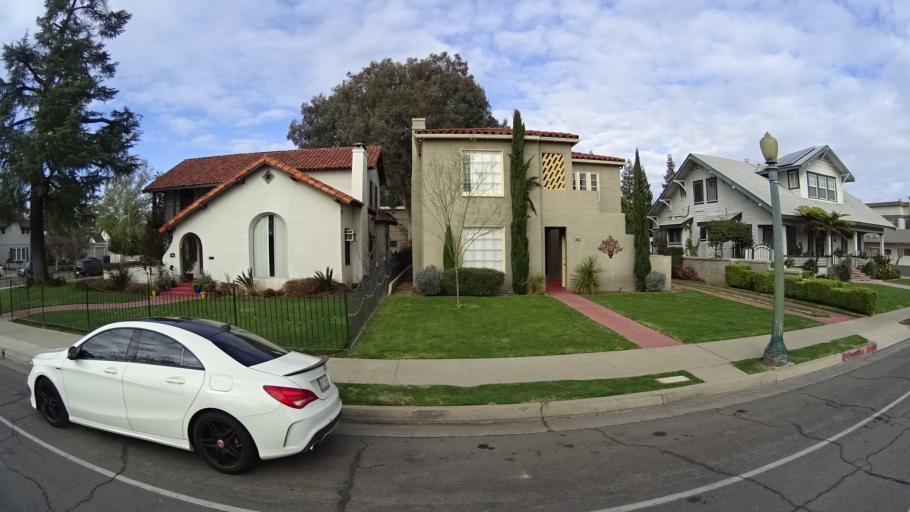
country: US
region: California
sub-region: Fresno County
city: Fresno
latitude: 36.7637
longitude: -119.8011
